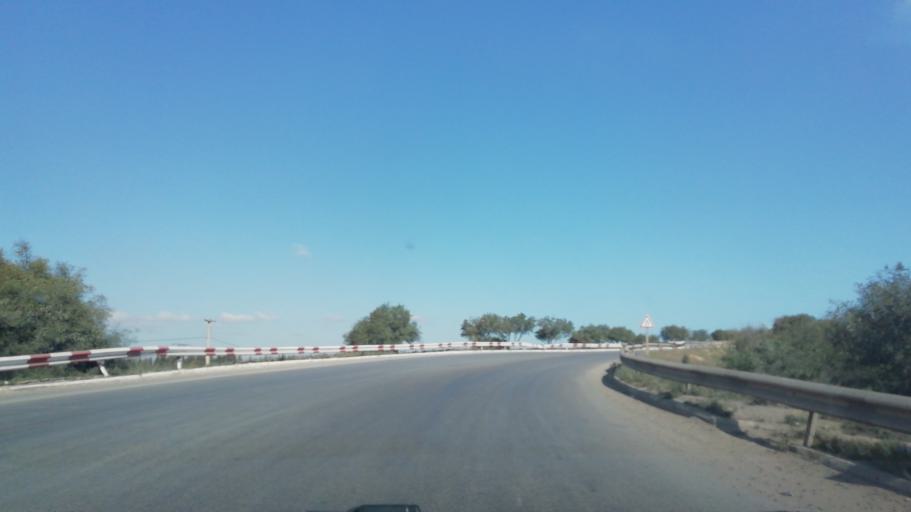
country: DZ
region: Oran
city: Ain el Bya
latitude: 35.7846
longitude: -0.2856
